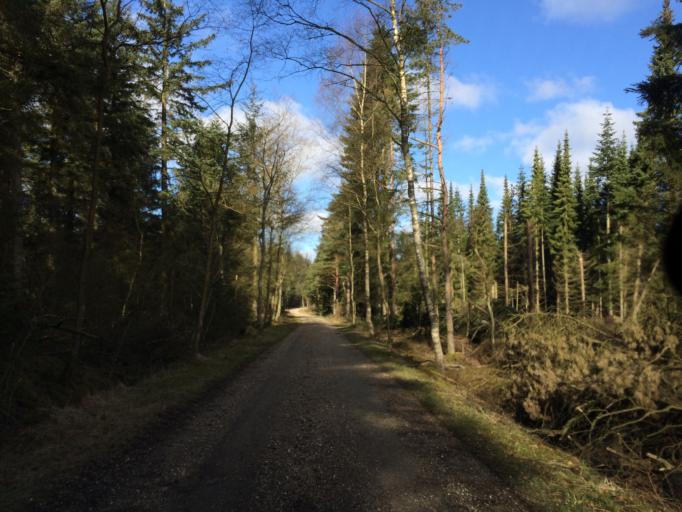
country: DK
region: Central Jutland
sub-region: Holstebro Kommune
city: Ulfborg
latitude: 56.2737
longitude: 8.4283
